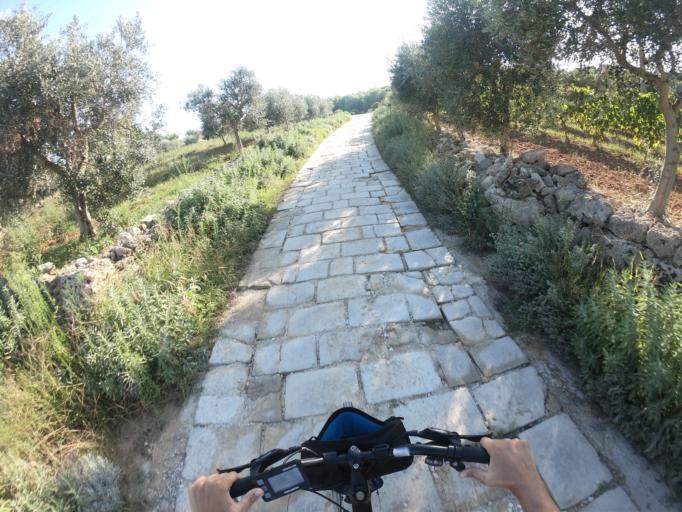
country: IT
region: Apulia
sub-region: Provincia di Lecce
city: Supersano
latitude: 40.0434
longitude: 18.2135
